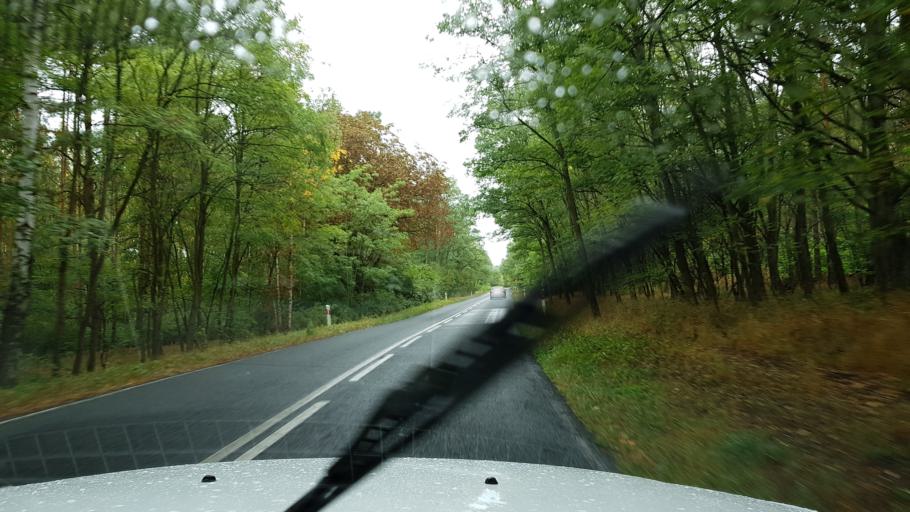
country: PL
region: West Pomeranian Voivodeship
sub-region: Powiat gryfinski
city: Cedynia
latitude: 52.8375
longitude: 14.1275
